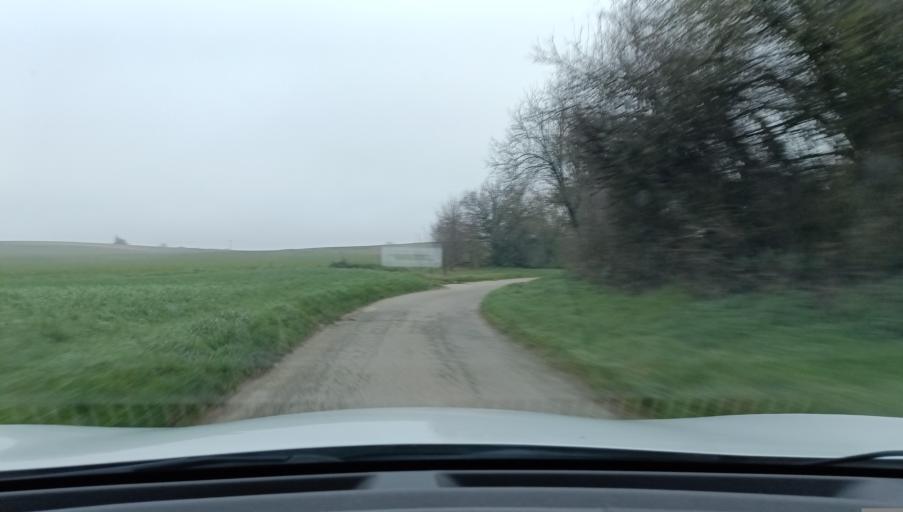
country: FR
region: Rhone-Alpes
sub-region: Departement de l'Isere
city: Seyssuel
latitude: 45.5801
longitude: 4.8485
